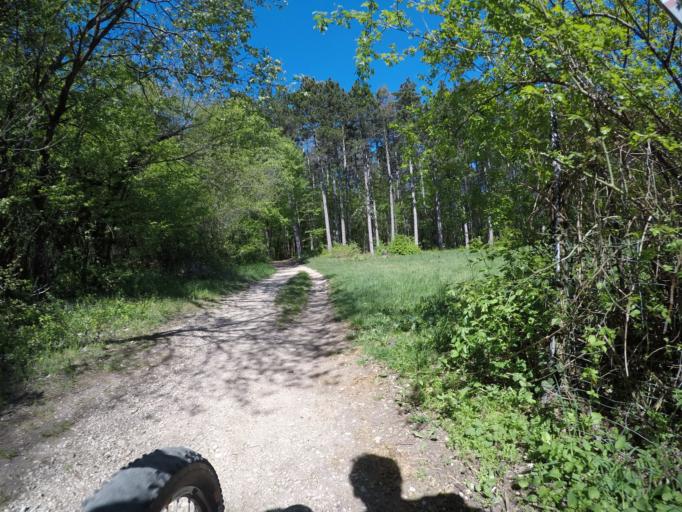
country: AT
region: Lower Austria
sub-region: Politischer Bezirk Modling
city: Gumpoldskirchen
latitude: 48.0517
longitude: 16.2667
